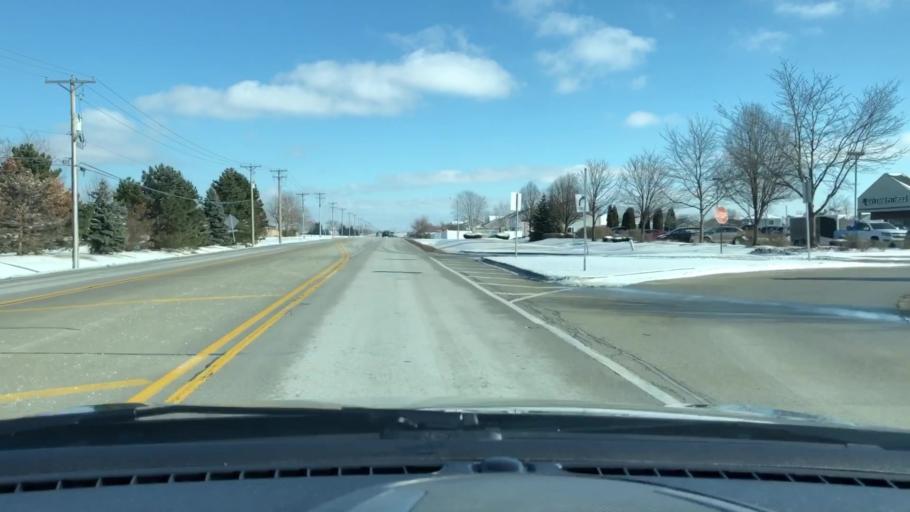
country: US
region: Illinois
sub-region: Will County
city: New Lenox
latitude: 41.4828
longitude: -87.9819
